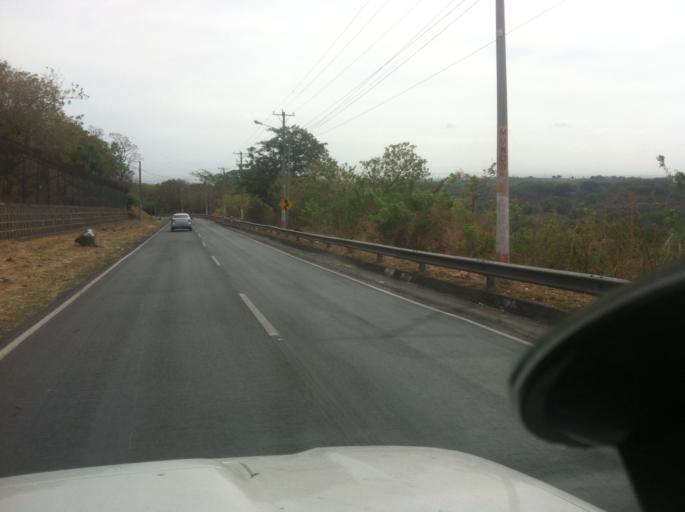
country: NI
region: Managua
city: Ciudad Sandino
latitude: 12.0990
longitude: -86.3224
